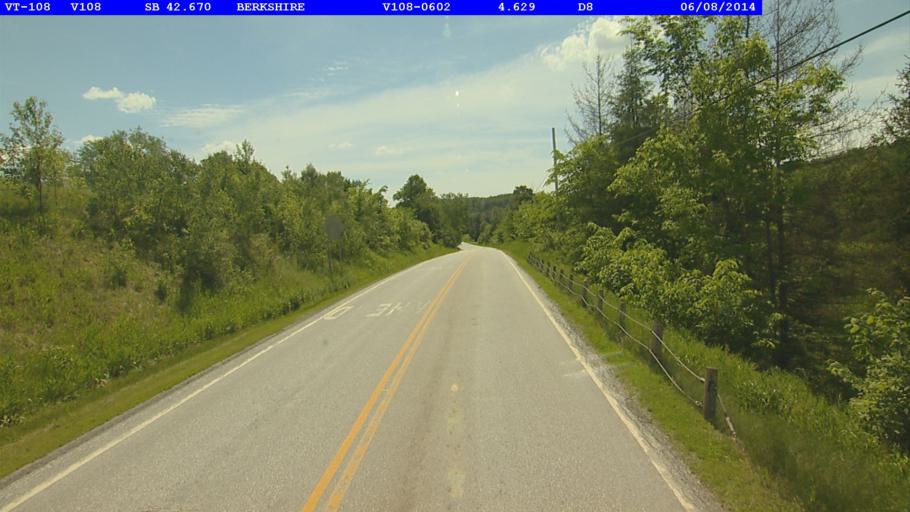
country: US
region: Vermont
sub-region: Franklin County
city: Enosburg Falls
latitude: 44.9874
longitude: -72.8153
